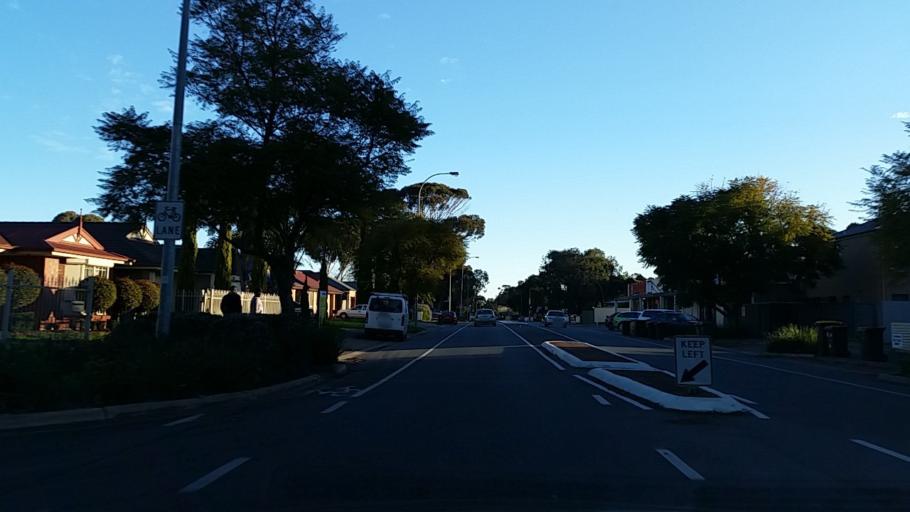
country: AU
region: South Australia
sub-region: Salisbury
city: Salisbury
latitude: -34.7510
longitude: 138.6356
